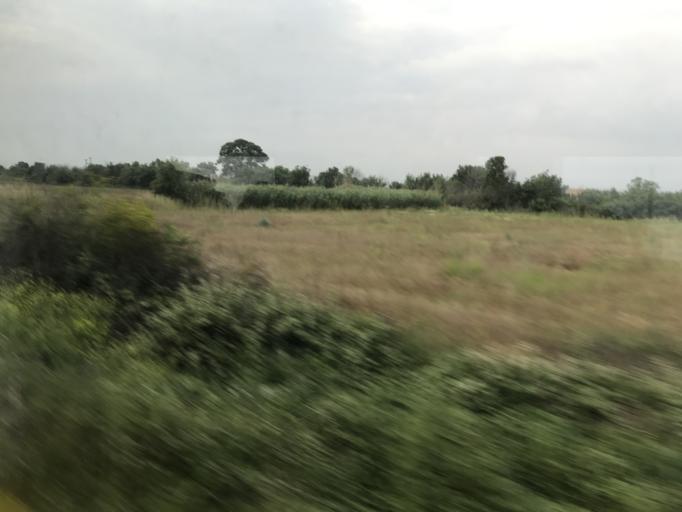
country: GR
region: East Macedonia and Thrace
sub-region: Nomos Rodopis
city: Arisvi
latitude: 41.0455
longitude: 25.6366
